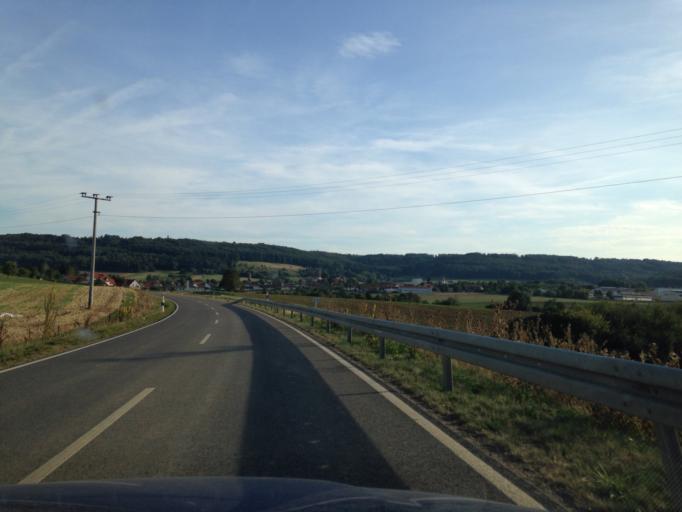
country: DE
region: Bavaria
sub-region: Regierungsbezirk Mittelfranken
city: Thalmassing
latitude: 49.0982
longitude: 11.2178
